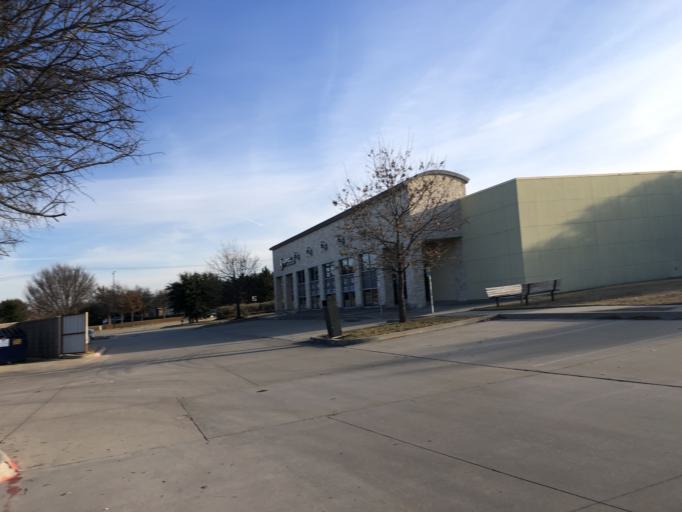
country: US
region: Texas
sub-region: Collin County
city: Frisco
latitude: 33.1185
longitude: -96.8020
